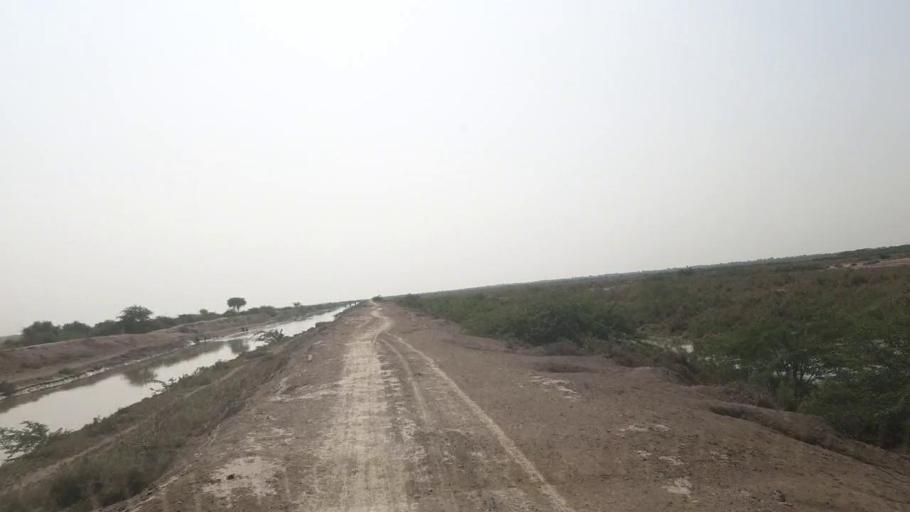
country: PK
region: Sindh
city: Kadhan
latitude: 24.3864
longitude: 68.9003
